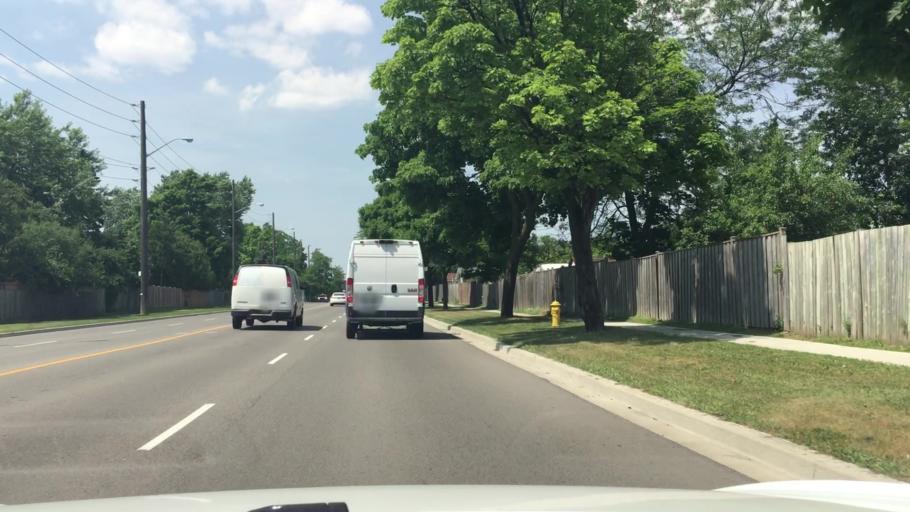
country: CA
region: Ontario
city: Scarborough
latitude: 43.7755
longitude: -79.2955
